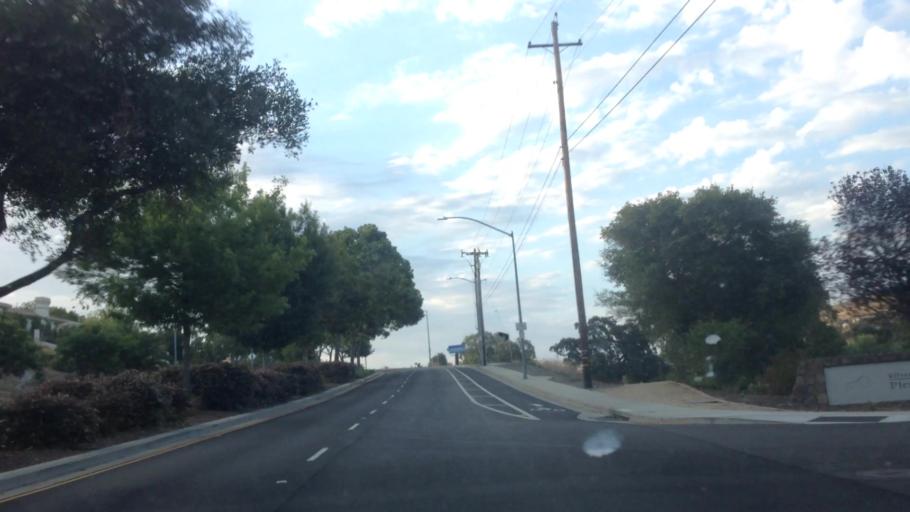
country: US
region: California
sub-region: Santa Clara County
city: Seven Trees
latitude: 37.2961
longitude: -121.7906
